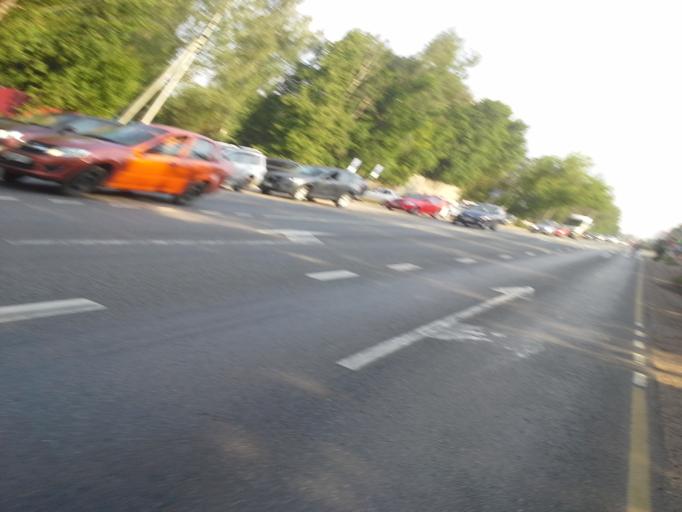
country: RU
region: Moskovskaya
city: Istra
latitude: 55.9053
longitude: 36.9450
